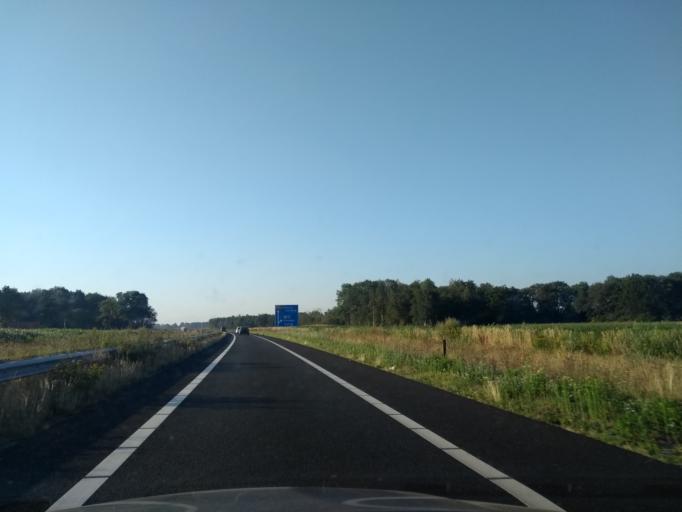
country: NL
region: Gelderland
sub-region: Berkelland
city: Eibergen
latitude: 52.0953
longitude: 6.6220
